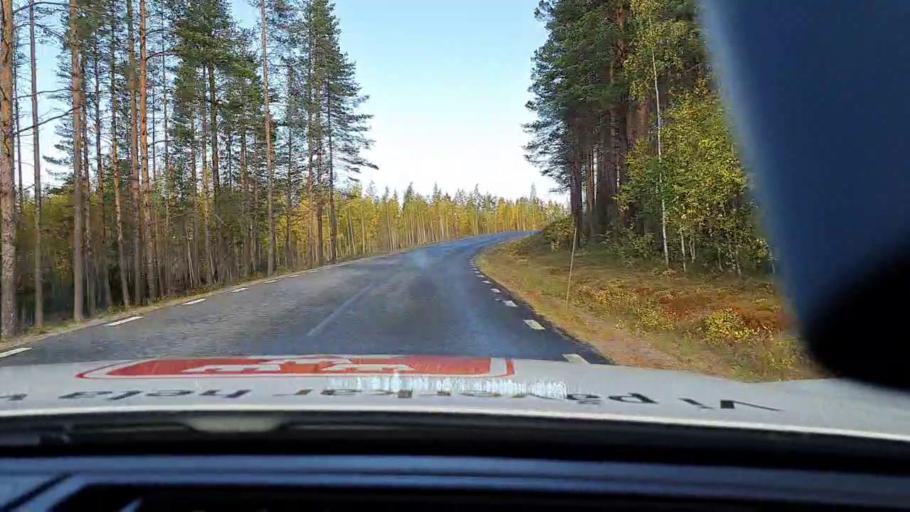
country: SE
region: Vaesterbotten
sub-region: Skelleftea Kommun
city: Langsele
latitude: 64.9488
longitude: 20.0223
